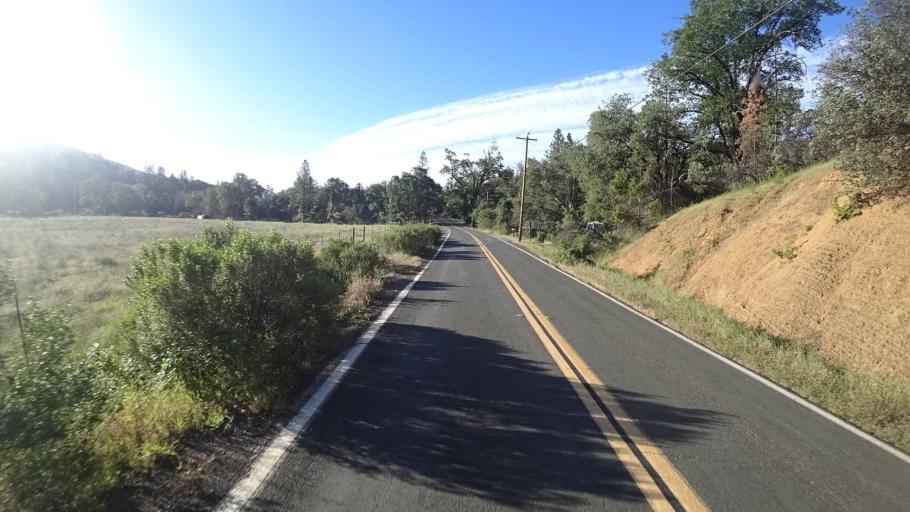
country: US
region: California
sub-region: Lake County
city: Upper Lake
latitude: 39.2102
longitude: -122.9295
